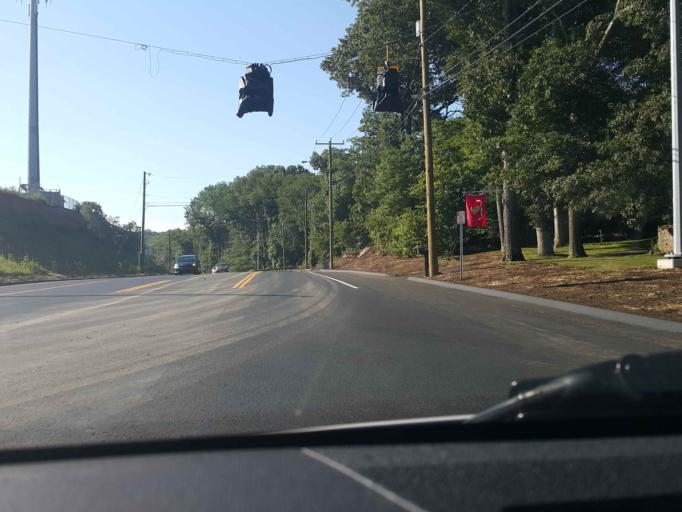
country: US
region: Connecticut
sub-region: New Haven County
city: Guilford
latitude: 41.3012
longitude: -72.7091
